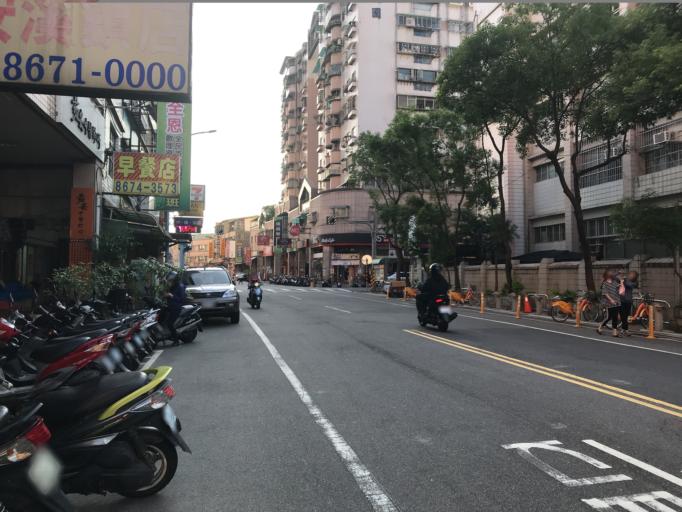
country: TW
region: Taiwan
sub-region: Taoyuan
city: Taoyuan
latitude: 24.9310
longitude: 121.3726
